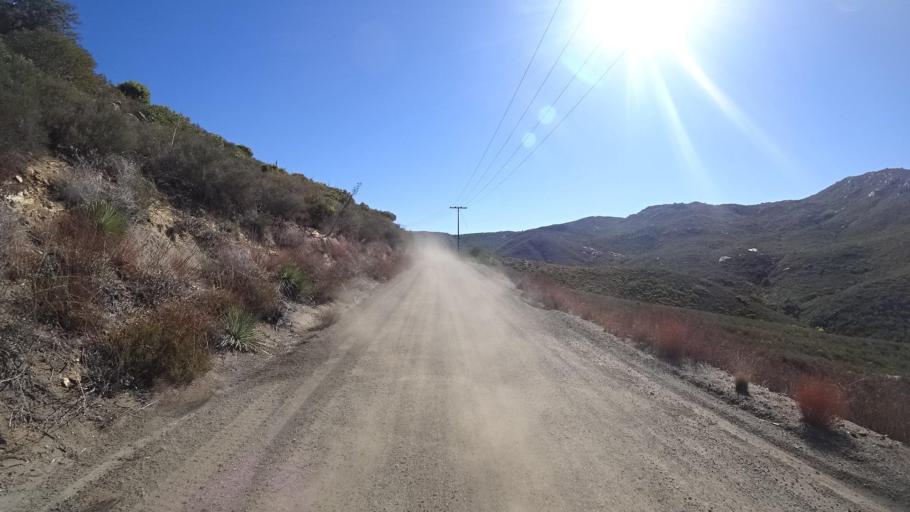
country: US
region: California
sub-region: San Diego County
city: Descanso
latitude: 32.8636
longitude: -116.6647
